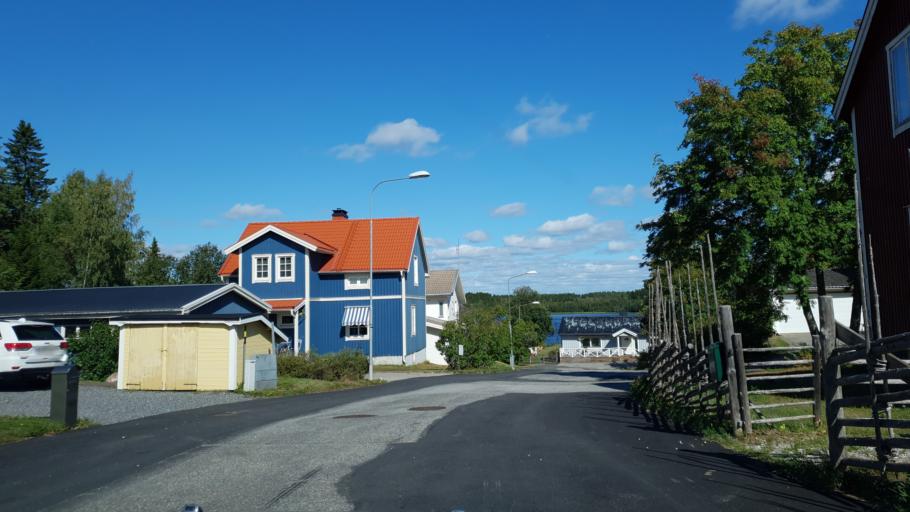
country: SE
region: Vaesterbotten
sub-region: Umea Kommun
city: Holmsund
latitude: 63.7179
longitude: 20.3814
